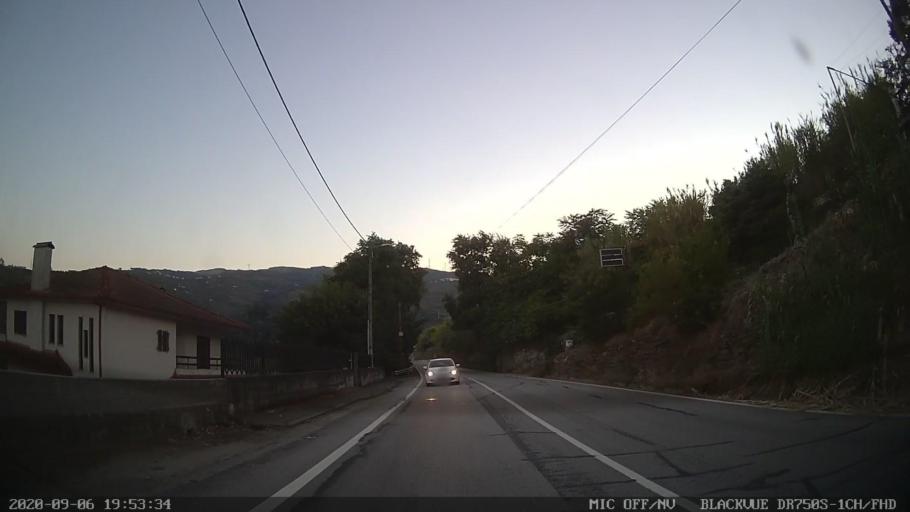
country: PT
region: Vila Real
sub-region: Peso da Regua
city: Godim
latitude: 41.1521
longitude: -7.8074
